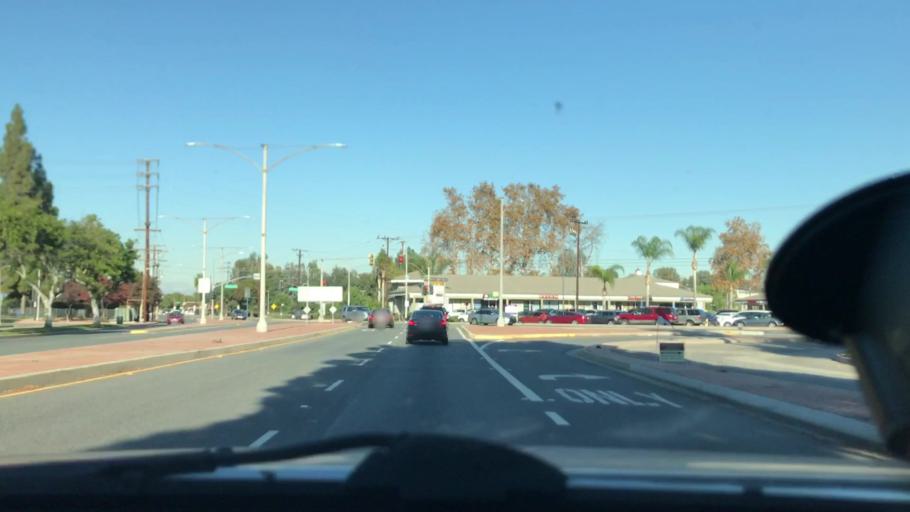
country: US
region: California
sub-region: Los Angeles County
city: Hawaiian Gardens
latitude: 33.8291
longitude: -118.1001
